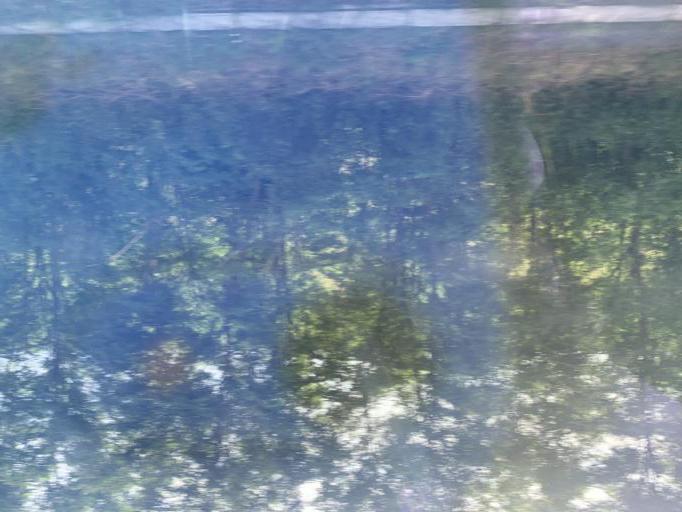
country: FR
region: Bourgogne
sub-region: Departement de Saone-et-Loire
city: Saint-Martin-Belle-Roche
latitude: 46.3597
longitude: 4.8500
